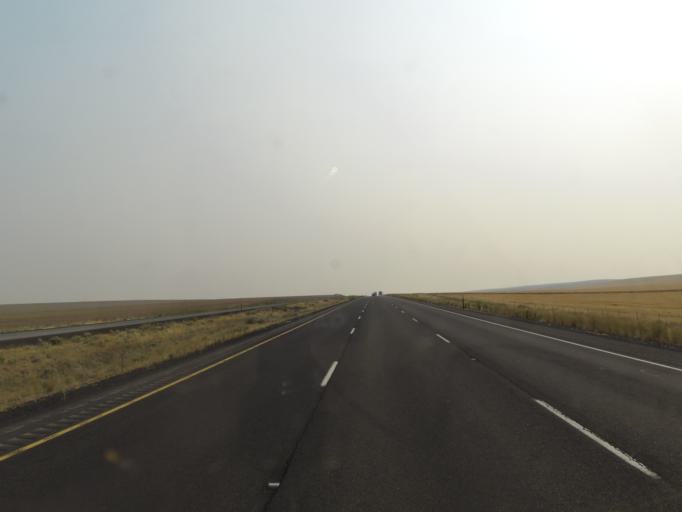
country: US
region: Washington
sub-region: Adams County
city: Ritzville
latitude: 46.9372
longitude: -118.5859
